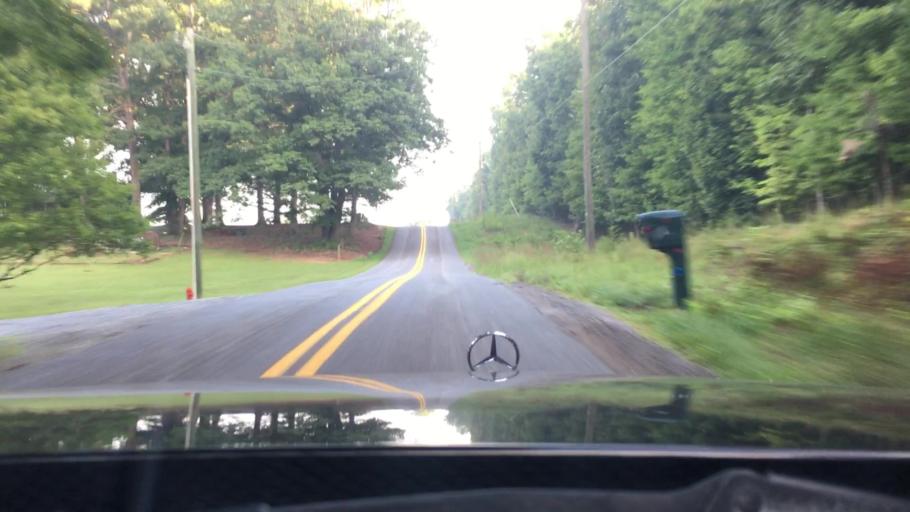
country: US
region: Virginia
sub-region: Campbell County
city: Timberlake
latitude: 37.2696
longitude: -79.2644
